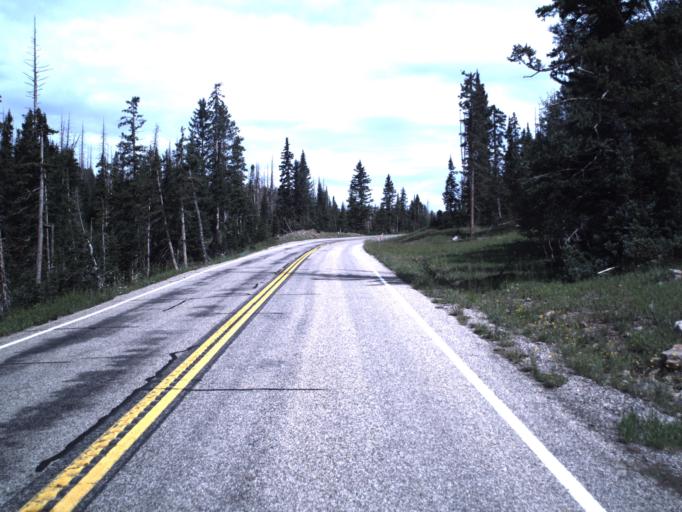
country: US
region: Utah
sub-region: Iron County
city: Cedar City
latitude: 37.5843
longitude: -112.8466
